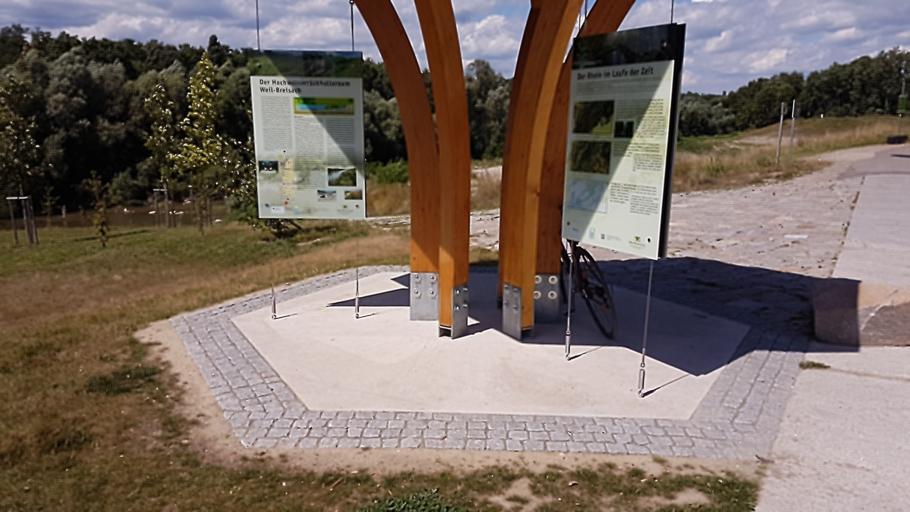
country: FR
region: Alsace
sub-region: Departement du Haut-Rhin
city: Chalampe
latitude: 47.8207
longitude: 7.5506
